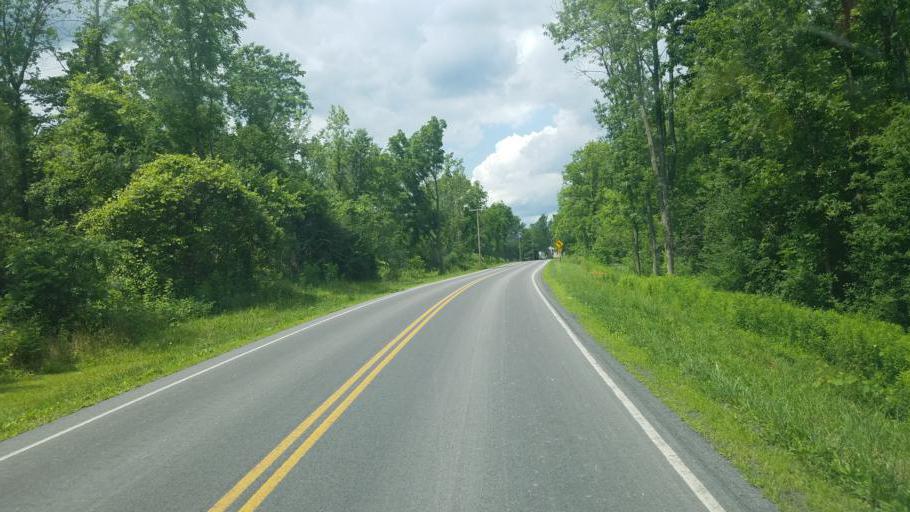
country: US
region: New York
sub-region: Wayne County
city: Clyde
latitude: 42.9977
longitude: -76.8720
